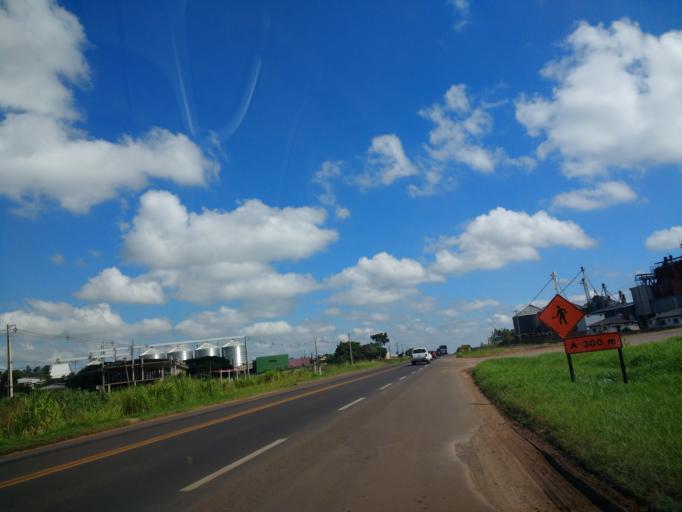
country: BR
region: Parana
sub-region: Umuarama
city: Umuarama
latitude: -23.8102
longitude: -53.3236
